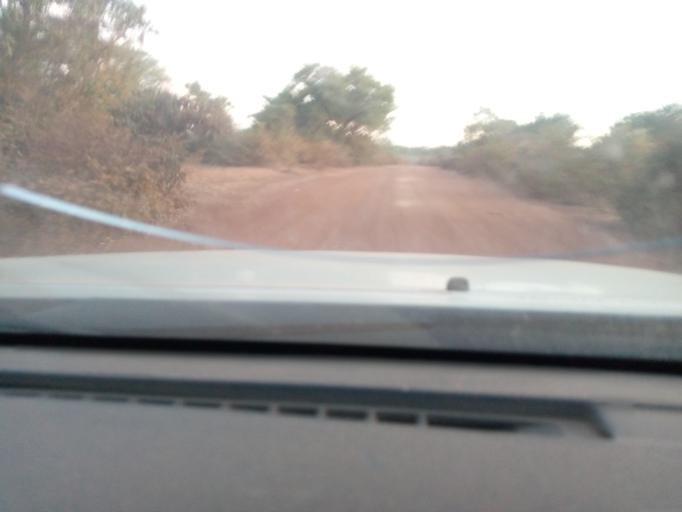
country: ML
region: Sikasso
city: Koutiala
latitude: 12.1037
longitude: -6.1445
